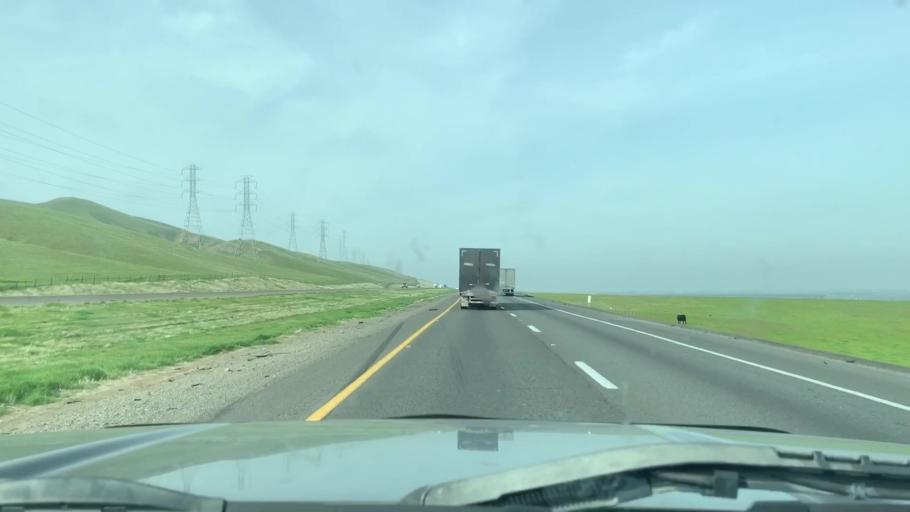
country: US
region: California
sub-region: Merced County
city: Los Banos
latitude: 36.8983
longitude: -120.8086
